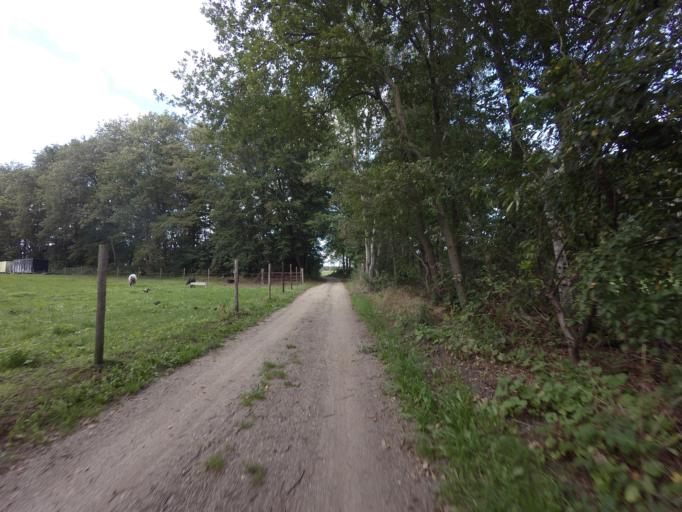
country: NL
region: Overijssel
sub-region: Gemeente Deventer
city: Schalkhaar
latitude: 52.2964
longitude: 6.2462
